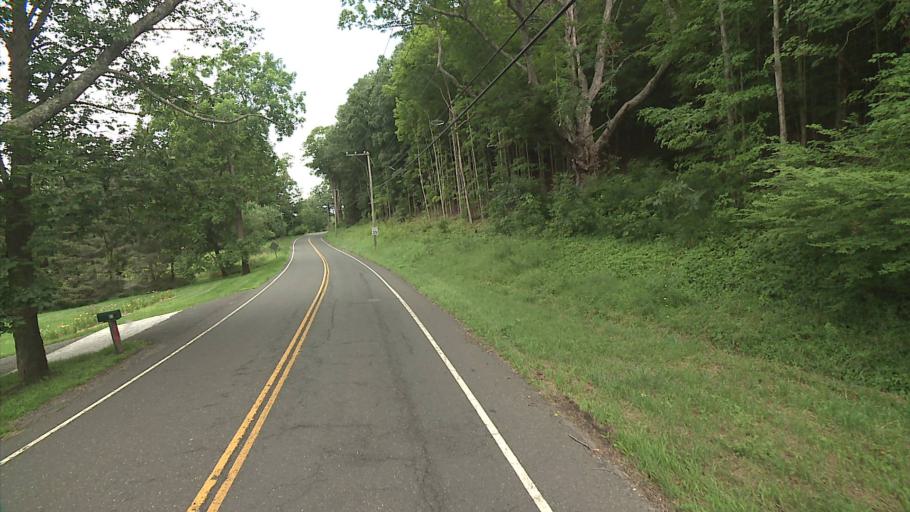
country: US
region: Connecticut
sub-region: Litchfield County
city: New Milford
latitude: 41.5636
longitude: -73.3120
